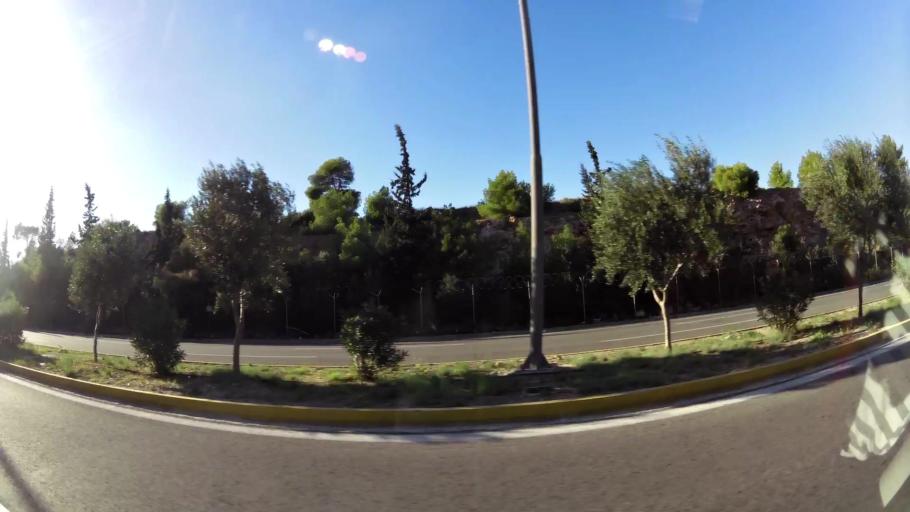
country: GR
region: Attica
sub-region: Nomarchia Athinas
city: Skaramangas
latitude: 38.0000
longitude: 23.6008
